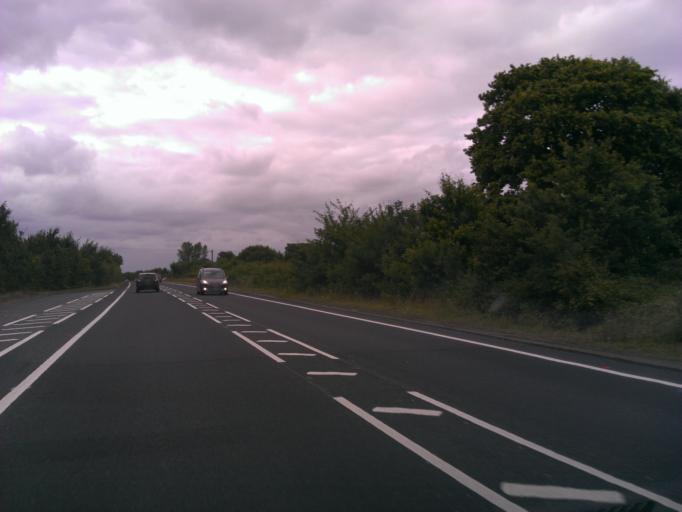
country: GB
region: England
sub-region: Essex
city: Little Clacton
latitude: 51.8326
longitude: 1.1278
